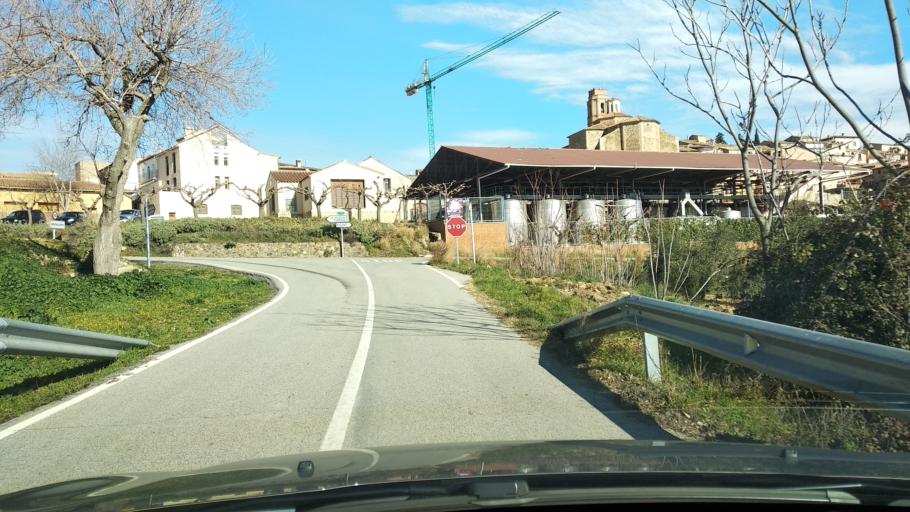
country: ES
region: Catalonia
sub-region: Provincia de Tarragona
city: Falset
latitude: 41.1916
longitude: 0.7759
